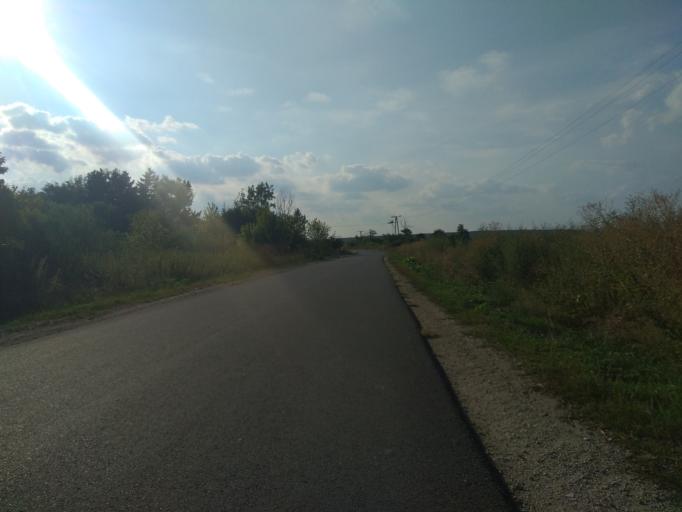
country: HU
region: Borsod-Abauj-Zemplen
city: Harsany
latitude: 47.8967
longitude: 20.7496
